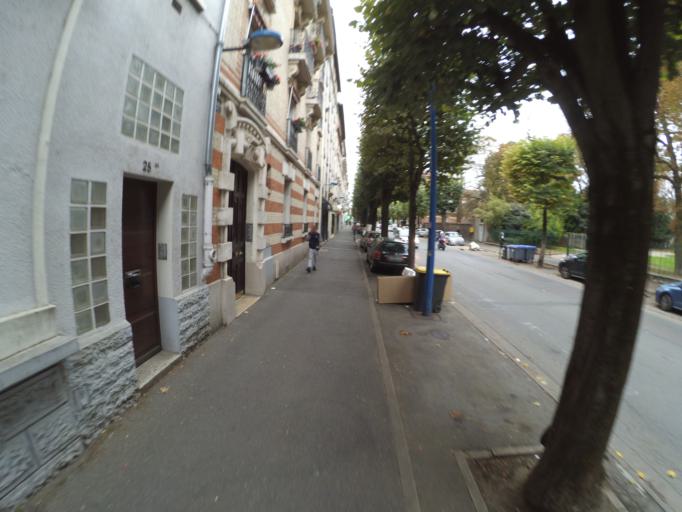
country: FR
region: Ile-de-France
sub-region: Departement du Val-de-Marne
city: Choisy-le-Roi
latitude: 48.7633
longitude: 2.4107
